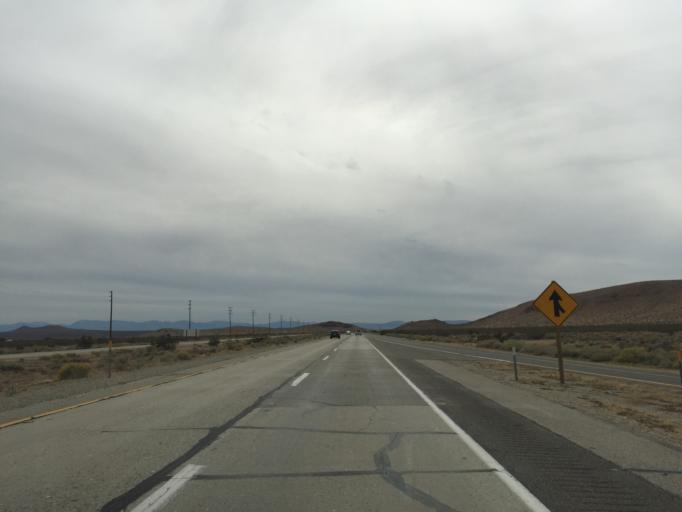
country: US
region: California
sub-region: Kern County
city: Mojave
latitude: 34.9923
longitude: -118.1598
